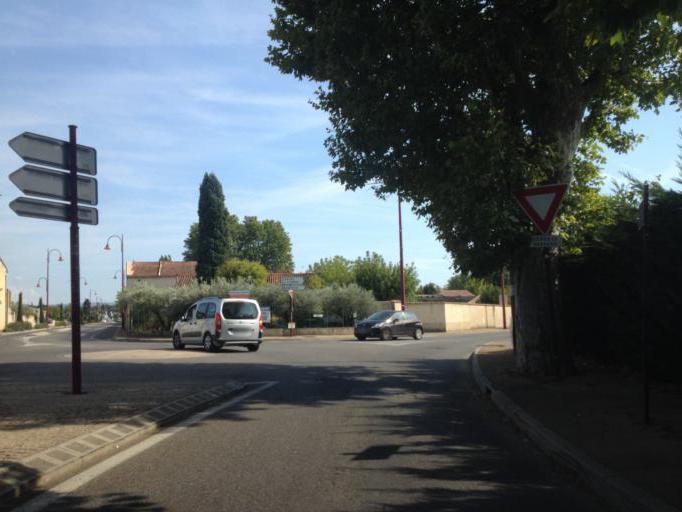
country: FR
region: Provence-Alpes-Cote d'Azur
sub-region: Departement du Vaucluse
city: Aubignan
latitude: 44.0957
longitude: 5.0266
